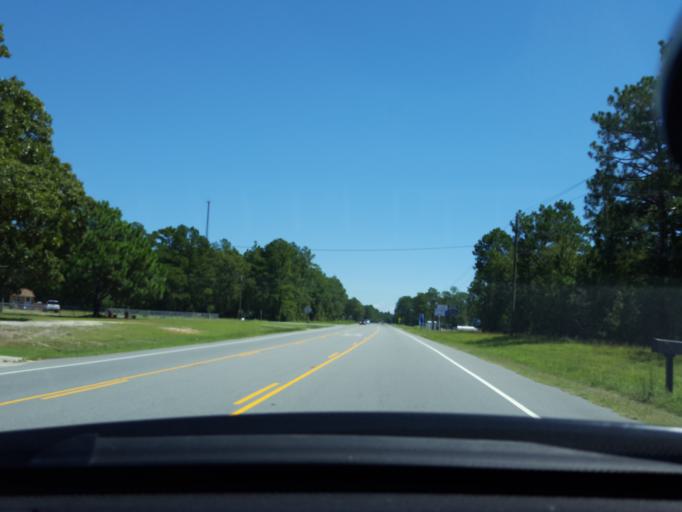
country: US
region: North Carolina
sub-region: Bladen County
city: Elizabethtown
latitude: 34.6474
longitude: -78.5527
